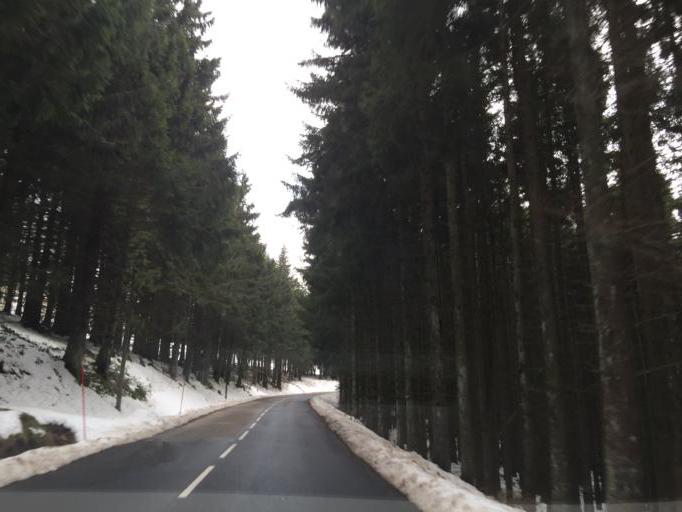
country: FR
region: Rhone-Alpes
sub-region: Departement de la Loire
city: Bourg-Argental
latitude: 45.3714
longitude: 4.5278
